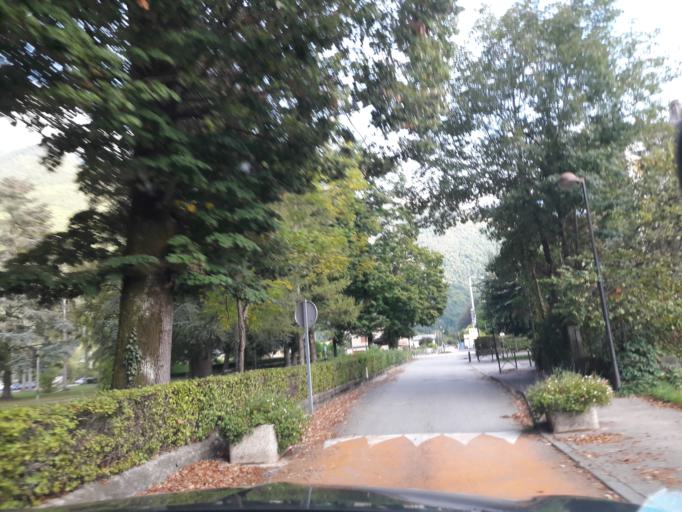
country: FR
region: Rhone-Alpes
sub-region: Departement de la Savoie
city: Aiton
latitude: 45.5451
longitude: 6.3017
